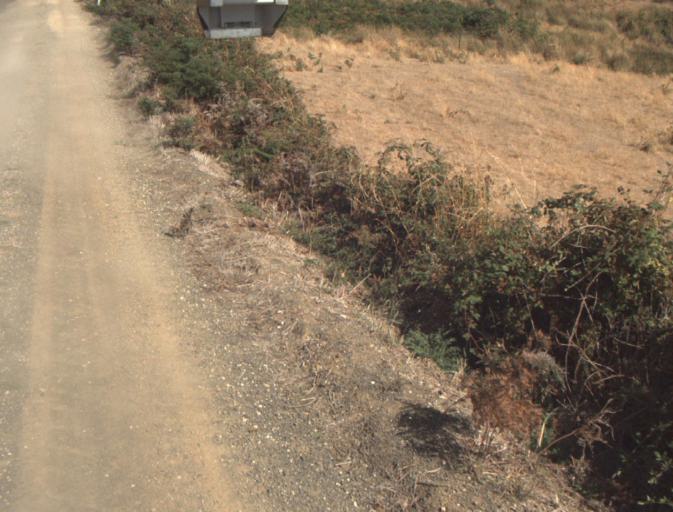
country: AU
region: Tasmania
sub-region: Launceston
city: Mayfield
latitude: -41.2078
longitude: 147.2216
